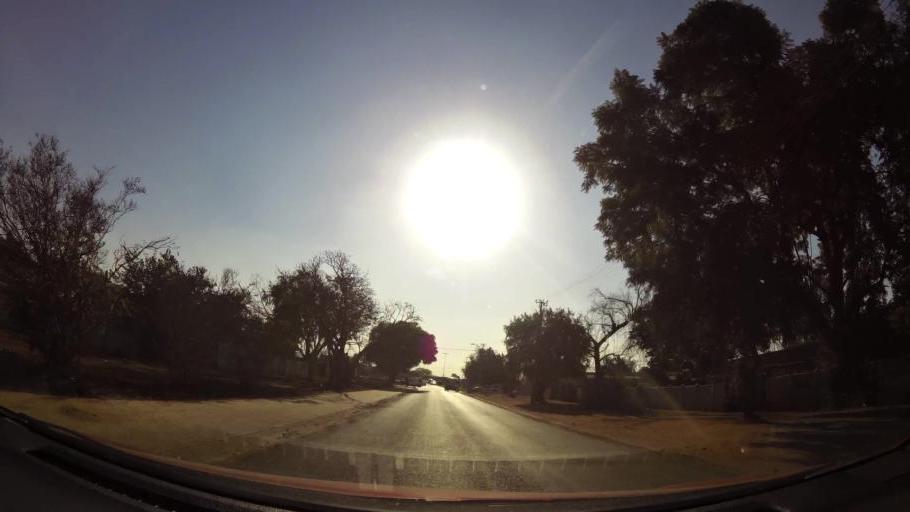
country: ZA
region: North-West
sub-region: Bojanala Platinum District Municipality
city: Rustenburg
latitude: -25.6493
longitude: 27.2266
